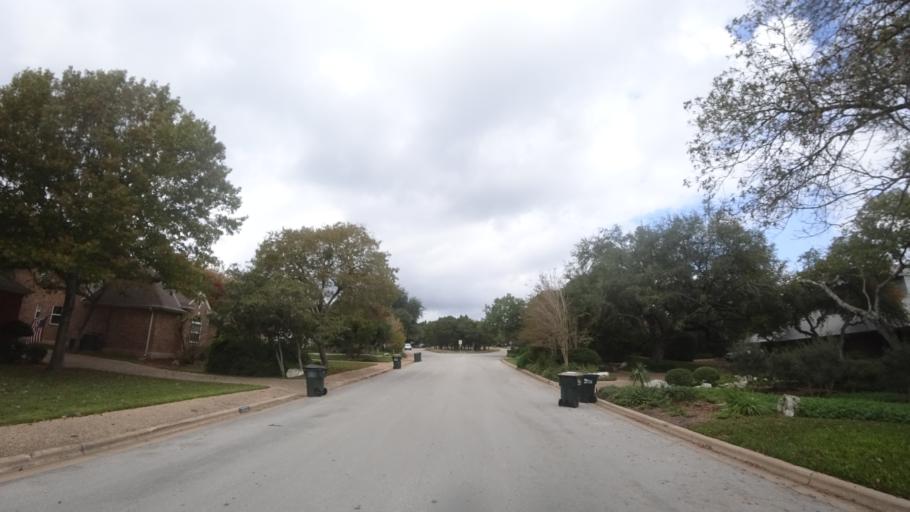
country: US
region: Texas
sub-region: Travis County
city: Barton Creek
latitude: 30.2908
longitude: -97.8836
